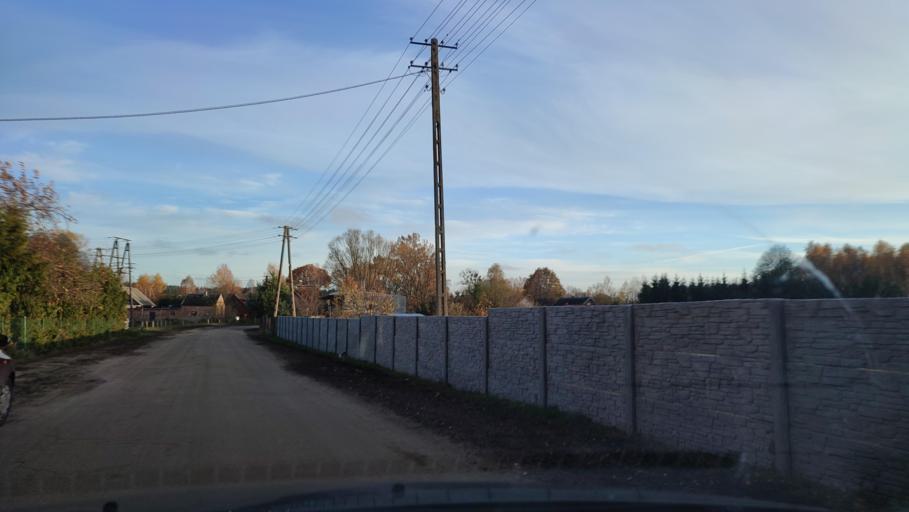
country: PL
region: Masovian Voivodeship
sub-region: Powiat mlawski
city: Dzierzgowo
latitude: 53.2782
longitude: 20.6470
